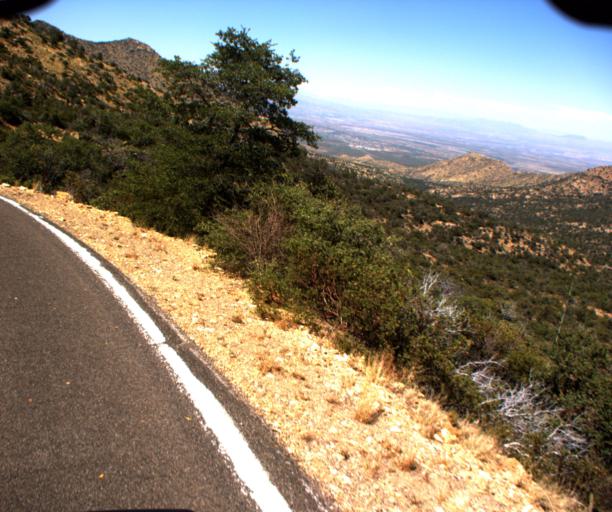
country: US
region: Arizona
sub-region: Graham County
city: Swift Trail Junction
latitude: 32.6576
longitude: -109.8042
